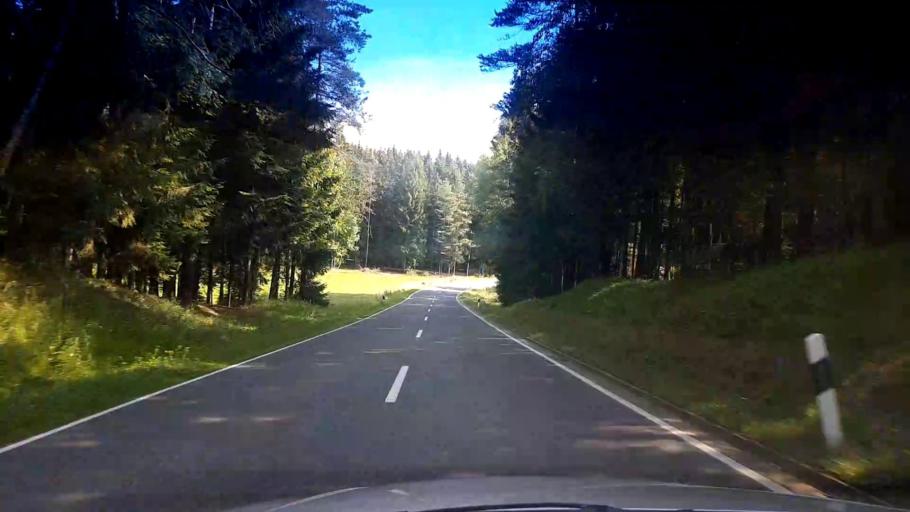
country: DE
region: Bavaria
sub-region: Upper Franconia
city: Stadelhofen
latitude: 49.9797
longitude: 11.2193
